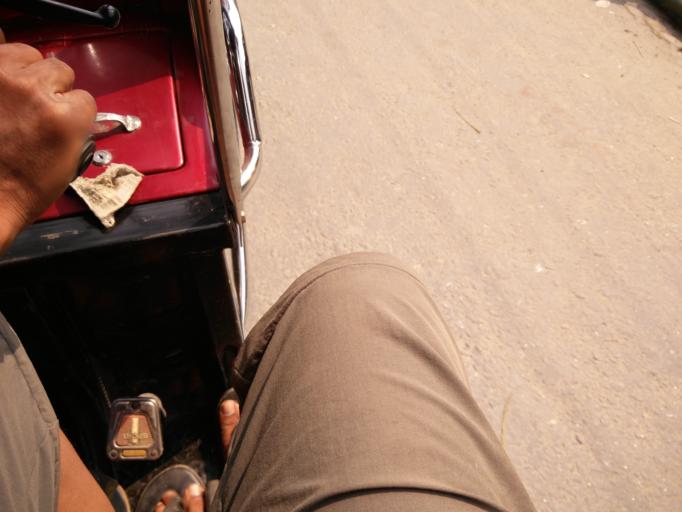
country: BD
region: Dhaka
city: Muktagacha
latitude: 24.9099
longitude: 90.2114
